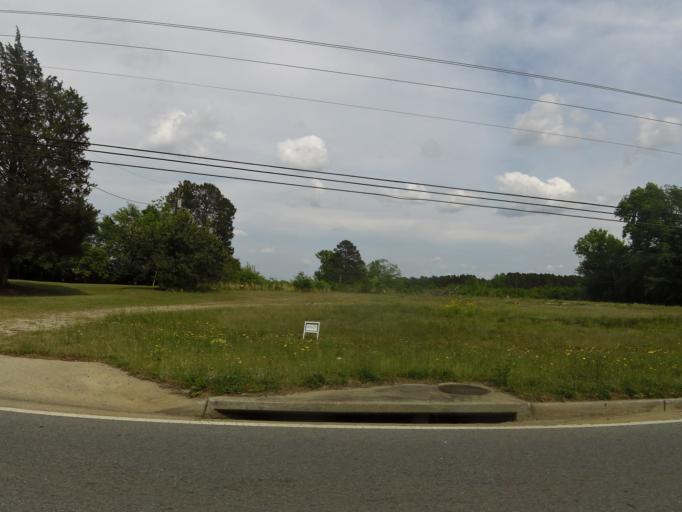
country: US
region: Georgia
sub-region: McDuffie County
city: Thomson
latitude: 33.5011
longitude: -82.5035
